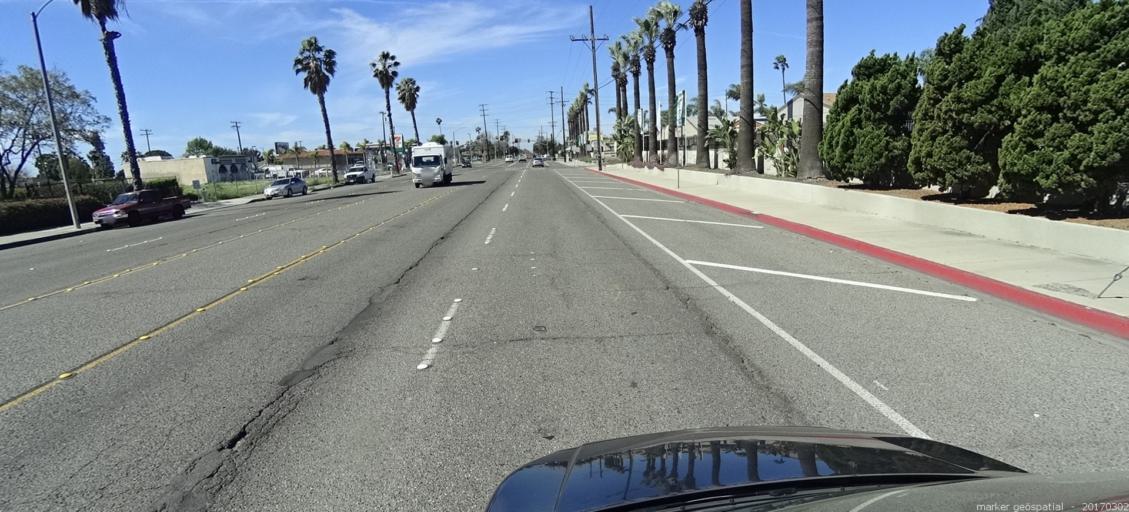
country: US
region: California
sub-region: Orange County
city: Placentia
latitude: 33.8473
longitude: -117.8785
